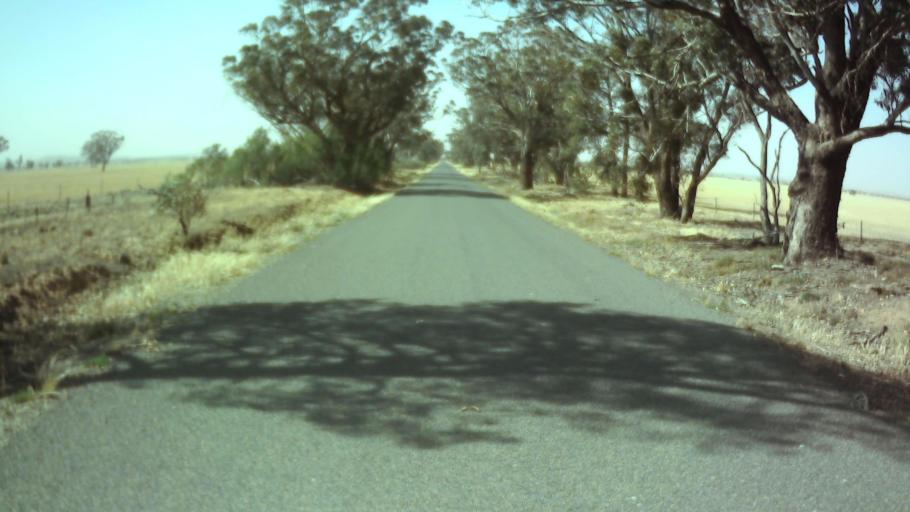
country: AU
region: New South Wales
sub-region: Weddin
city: Grenfell
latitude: -33.8921
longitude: 147.9223
